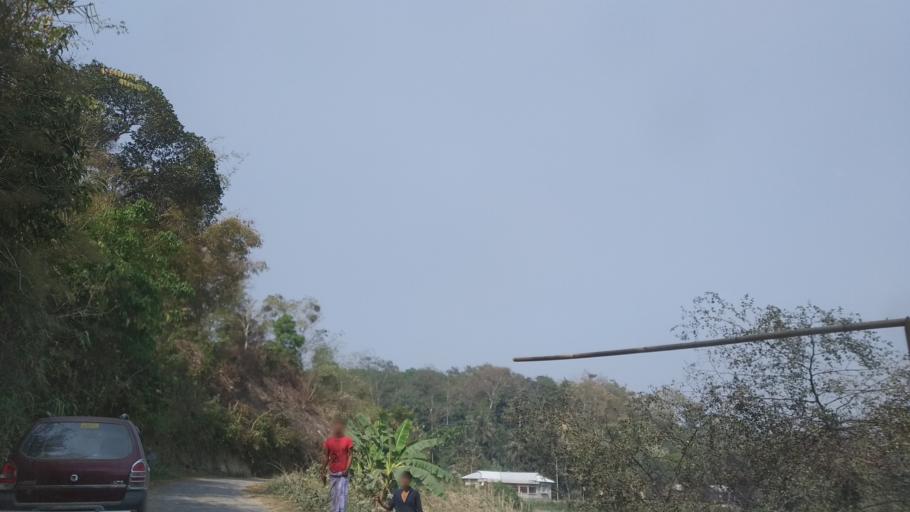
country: IN
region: Tripura
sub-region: West Tripura
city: Sonamura
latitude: 23.5232
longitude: 91.2589
